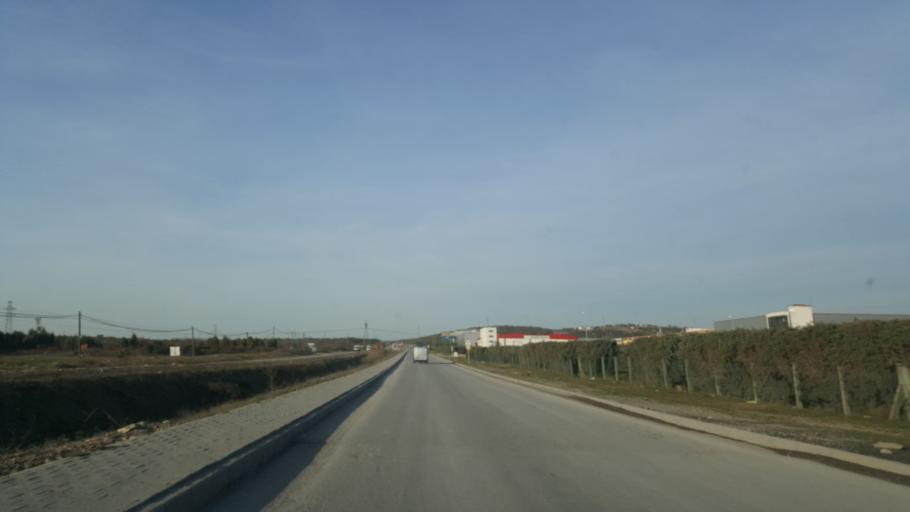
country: TR
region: Kocaeli
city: Tavsanli
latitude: 40.8558
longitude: 29.5563
